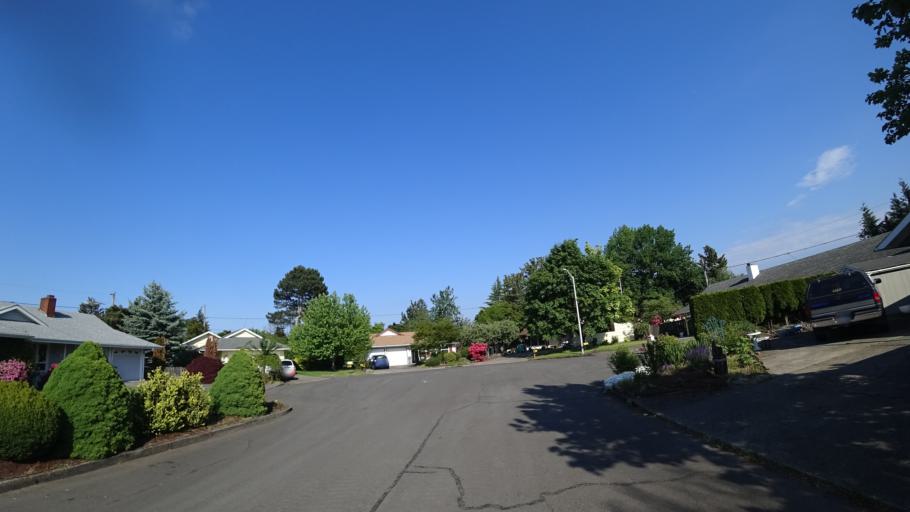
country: US
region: Oregon
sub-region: Multnomah County
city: Gresham
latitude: 45.5095
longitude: -122.5000
